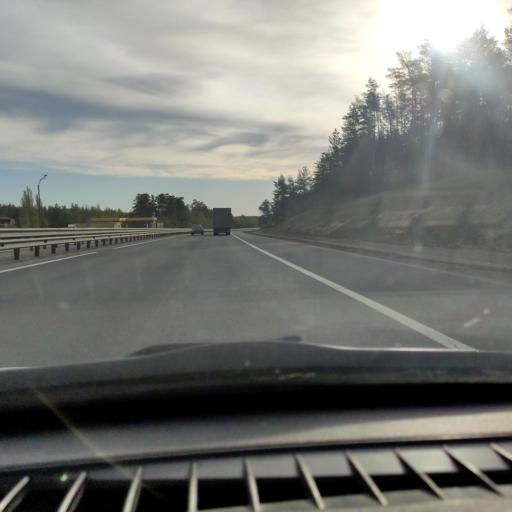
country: RU
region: Samara
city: Zhigulevsk
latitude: 53.5104
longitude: 49.5637
